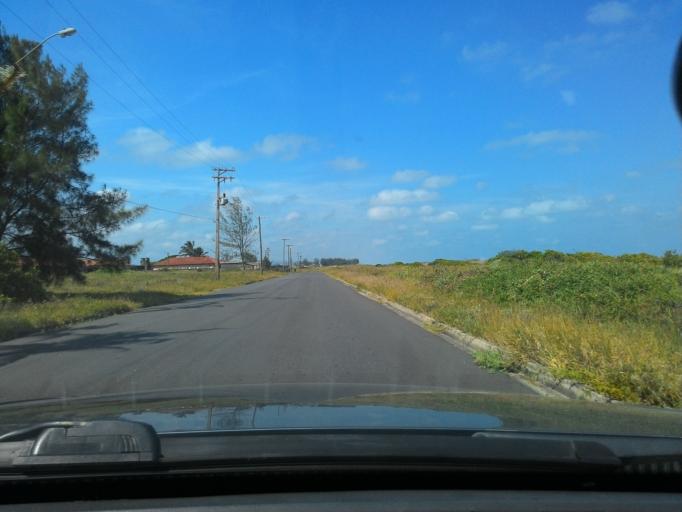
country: BR
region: Sao Paulo
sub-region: Iguape
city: Iguape
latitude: -24.8076
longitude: -47.6384
